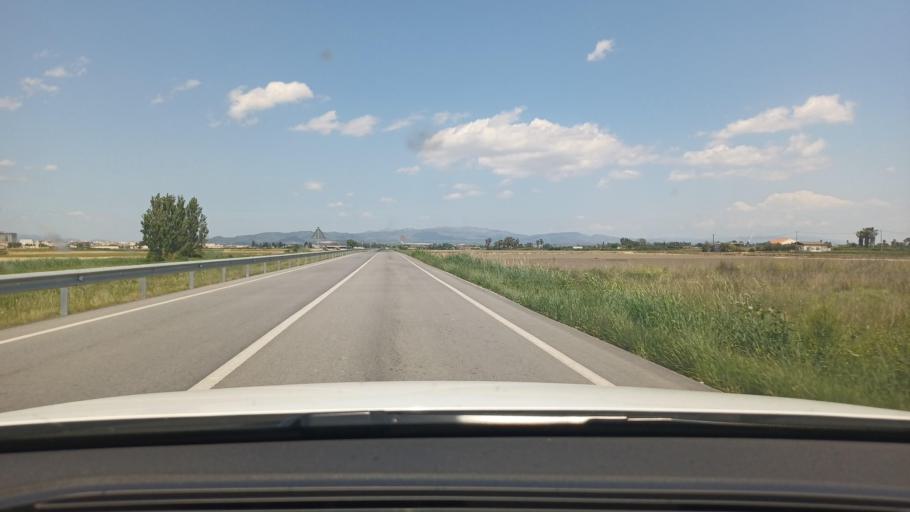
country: ES
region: Catalonia
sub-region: Provincia de Tarragona
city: Amposta
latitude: 40.6830
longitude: 0.5905
